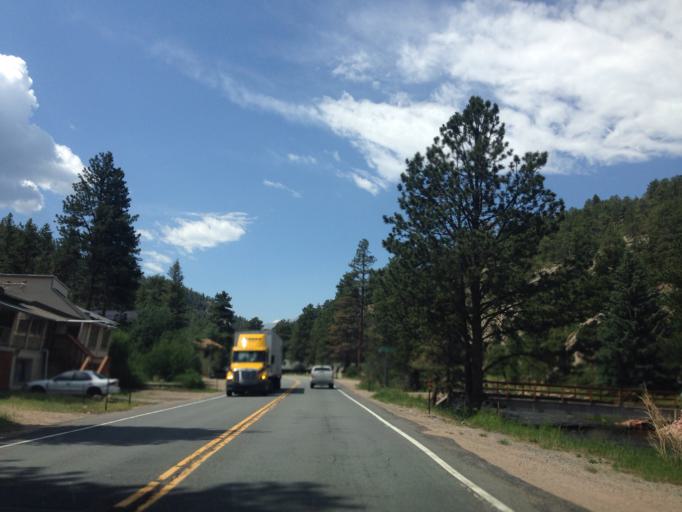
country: US
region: Colorado
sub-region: Larimer County
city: Estes Park
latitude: 40.3894
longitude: -105.4658
